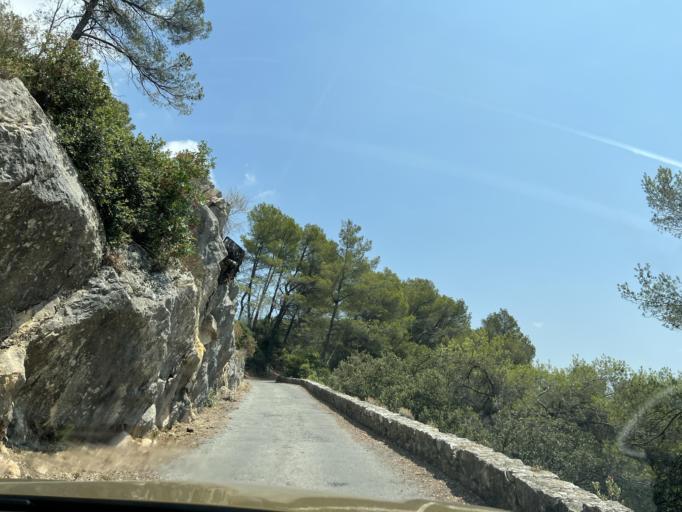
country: FR
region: Provence-Alpes-Cote d'Azur
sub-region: Departement des Alpes-Maritimes
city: Tourrettes-sur-Loup
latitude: 43.7039
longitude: 7.0371
